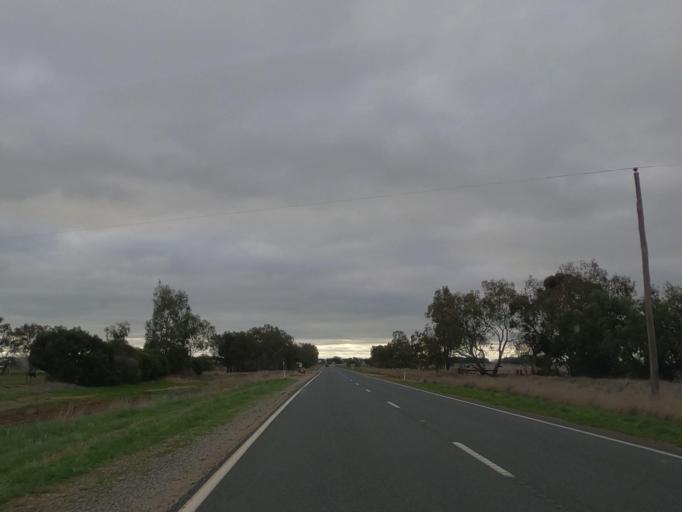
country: AU
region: Victoria
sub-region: Swan Hill
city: Swan Hill
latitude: -35.9387
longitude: 143.9361
